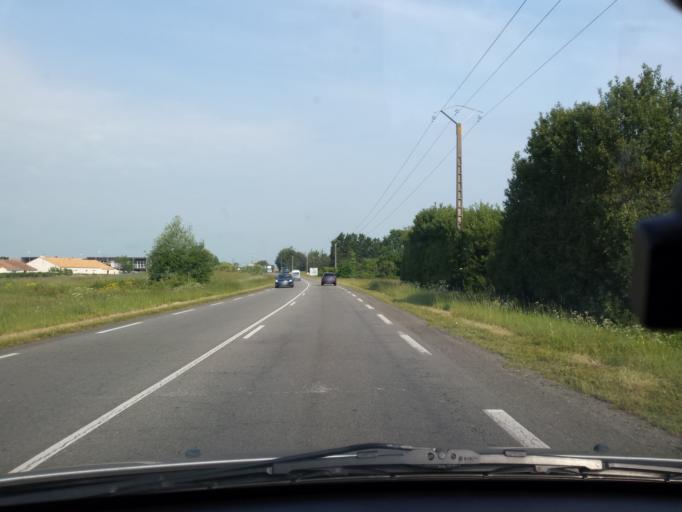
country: FR
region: Pays de la Loire
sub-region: Departement de la Loire-Atlantique
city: Machecoul
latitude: 46.9999
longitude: -1.8176
